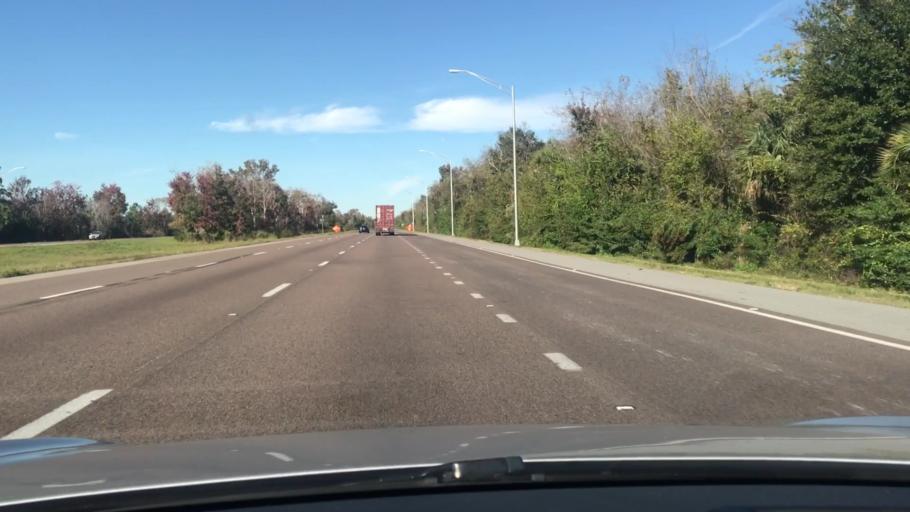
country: US
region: Florida
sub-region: Volusia County
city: Edgewater
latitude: 28.9558
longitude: -80.9527
